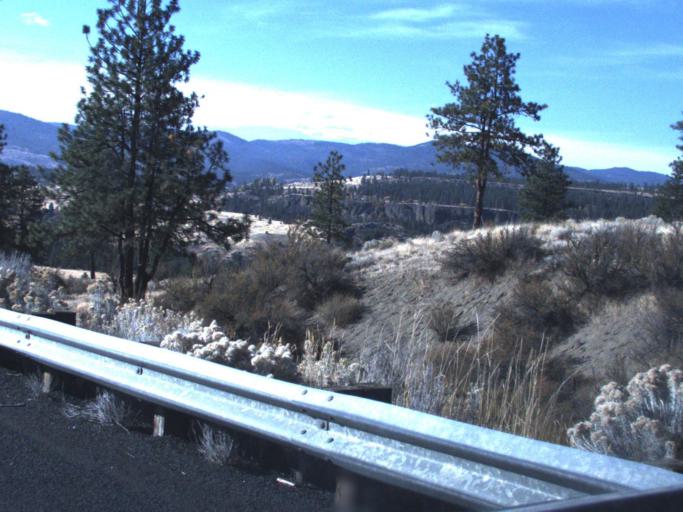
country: US
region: Washington
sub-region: Lincoln County
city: Davenport
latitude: 47.9086
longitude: -118.2868
